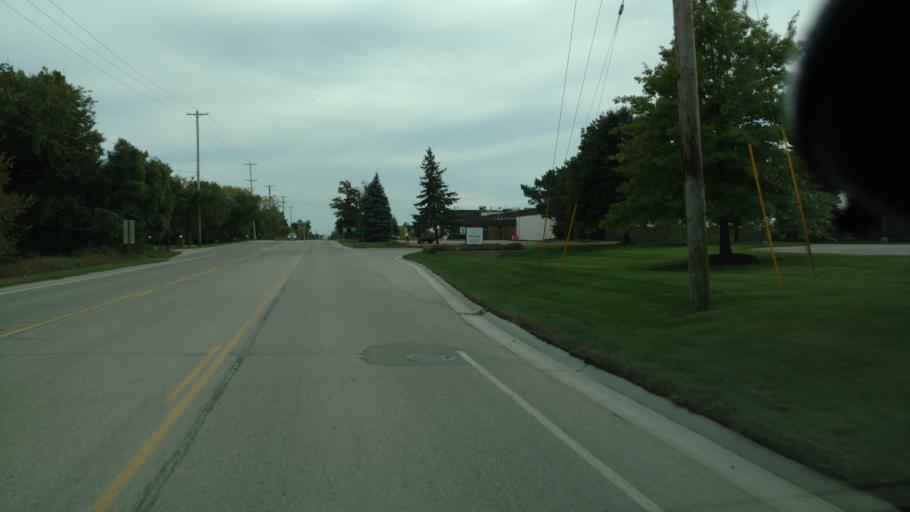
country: US
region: Michigan
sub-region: Ingham County
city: Lansing
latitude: 42.7702
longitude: -84.5231
